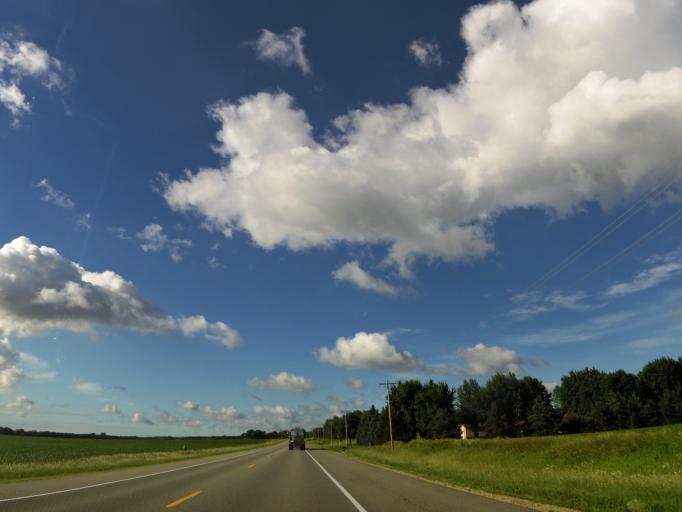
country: US
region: Minnesota
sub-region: Dakota County
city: Hastings
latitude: 44.7111
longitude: -92.8885
